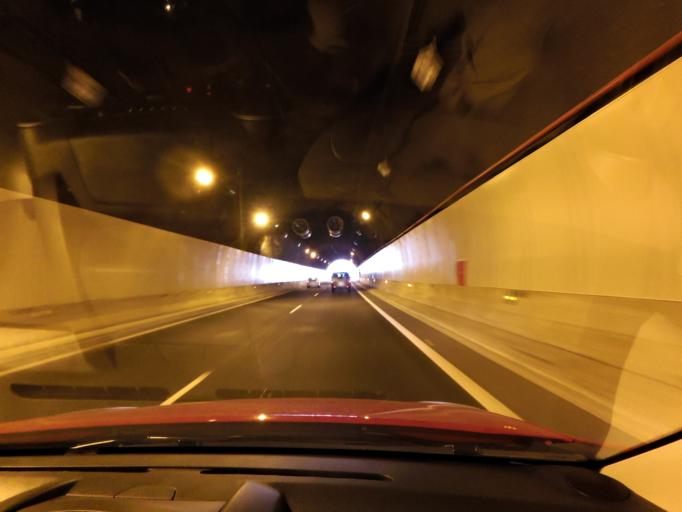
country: ES
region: Canary Islands
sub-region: Provincia de Las Palmas
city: Puerto Rico
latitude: 27.7867
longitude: -15.6888
